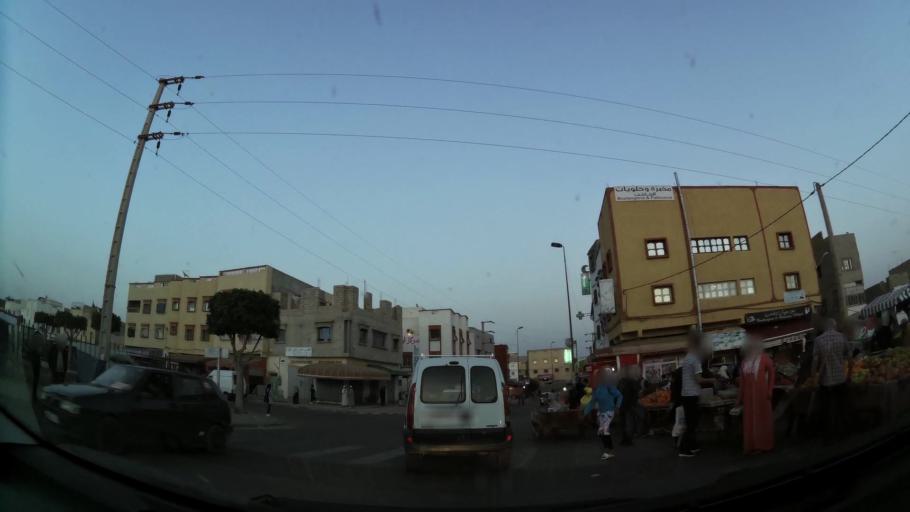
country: MA
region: Souss-Massa-Draa
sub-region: Inezgane-Ait Mellou
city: Inezgane
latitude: 30.3761
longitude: -9.4953
